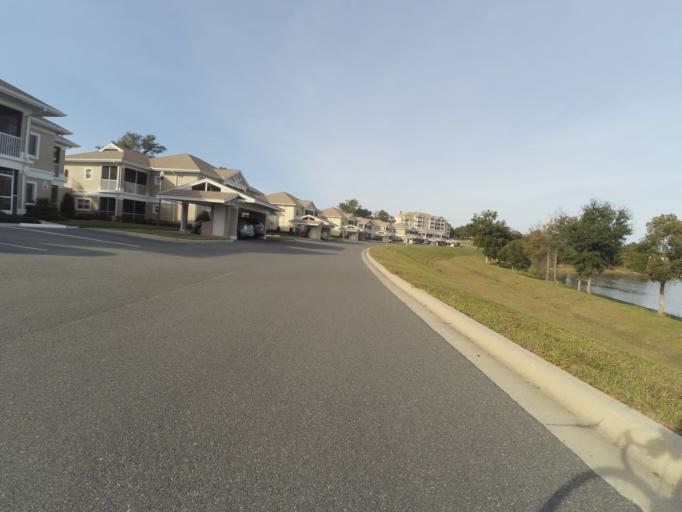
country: US
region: Florida
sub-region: Lake County
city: Umatilla
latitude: 28.9621
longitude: -81.6533
